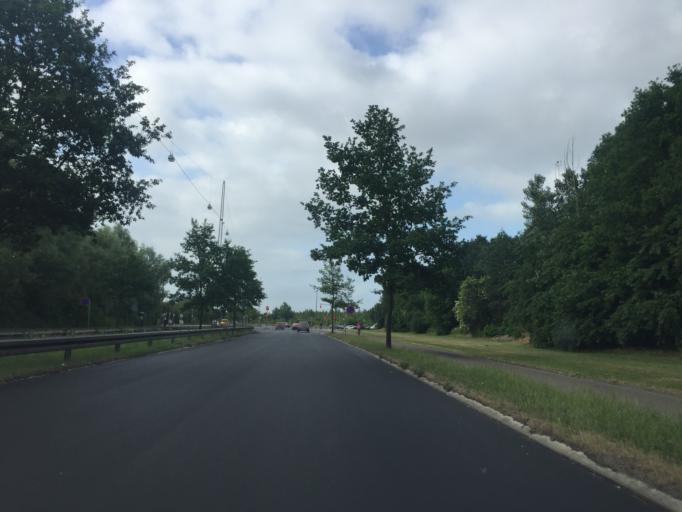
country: DK
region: Capital Region
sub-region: Hvidovre Kommune
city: Hvidovre
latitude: 55.6596
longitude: 12.4542
